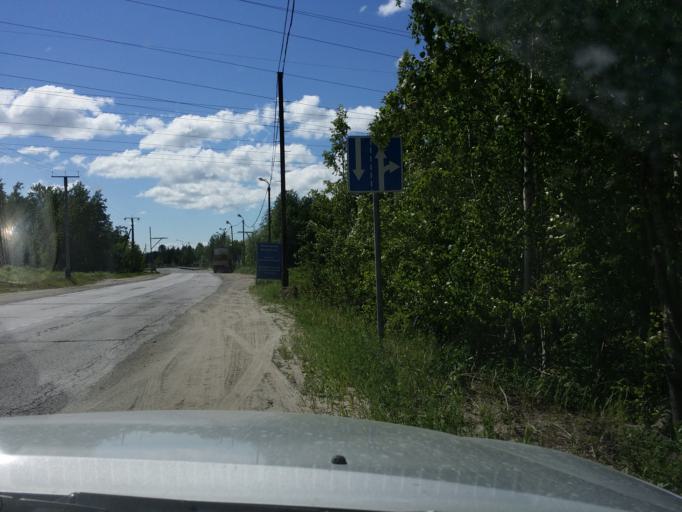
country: RU
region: Khanty-Mansiyskiy Avtonomnyy Okrug
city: Nizhnevartovsk
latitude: 61.0093
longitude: 76.4111
